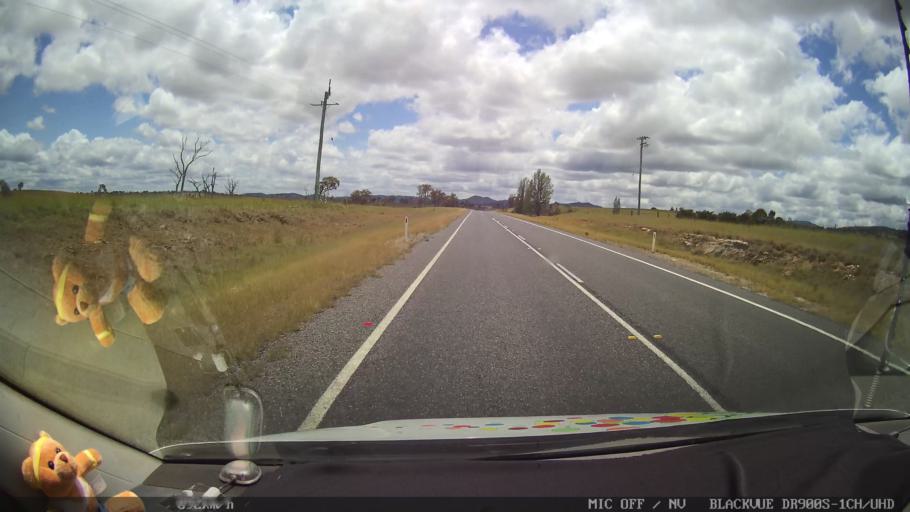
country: AU
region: New South Wales
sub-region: Glen Innes Severn
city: Glen Innes
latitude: -29.4154
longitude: 151.8648
